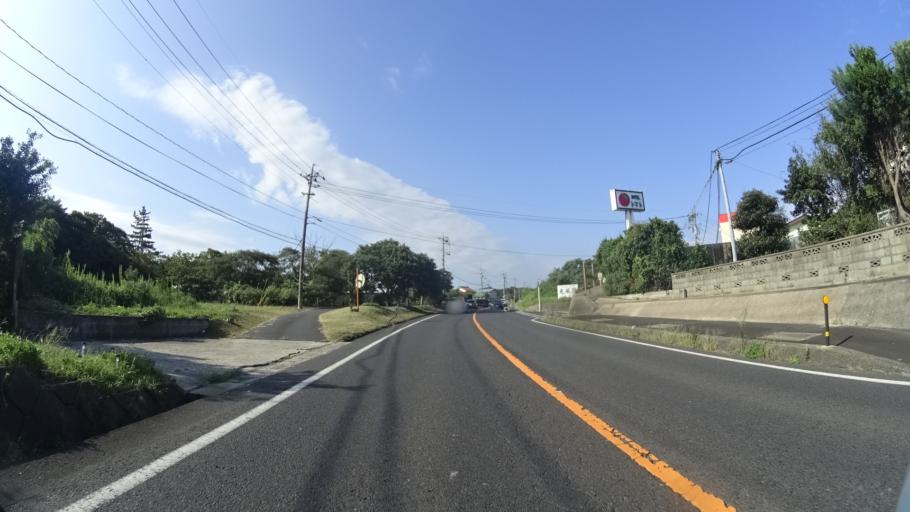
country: JP
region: Shimane
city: Izumo
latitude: 35.3091
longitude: 132.6589
